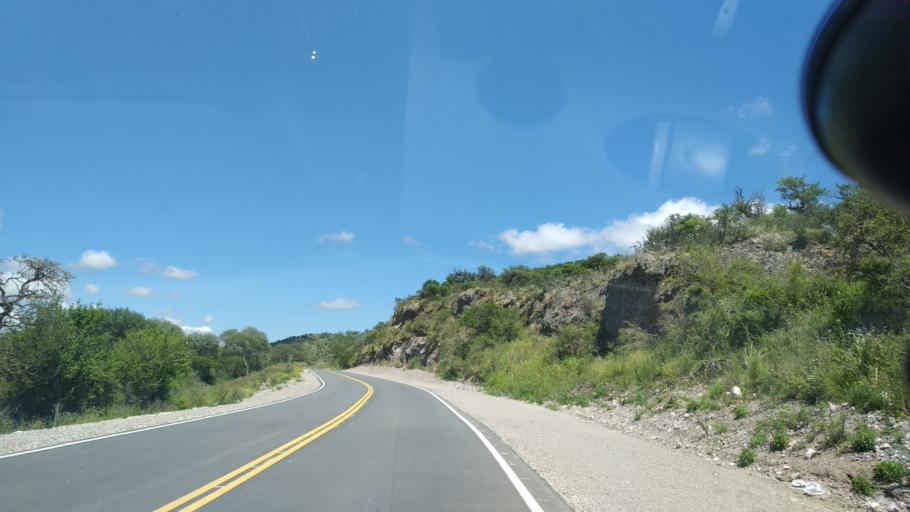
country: AR
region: Cordoba
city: Salsacate
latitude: -31.3458
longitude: -65.0942
